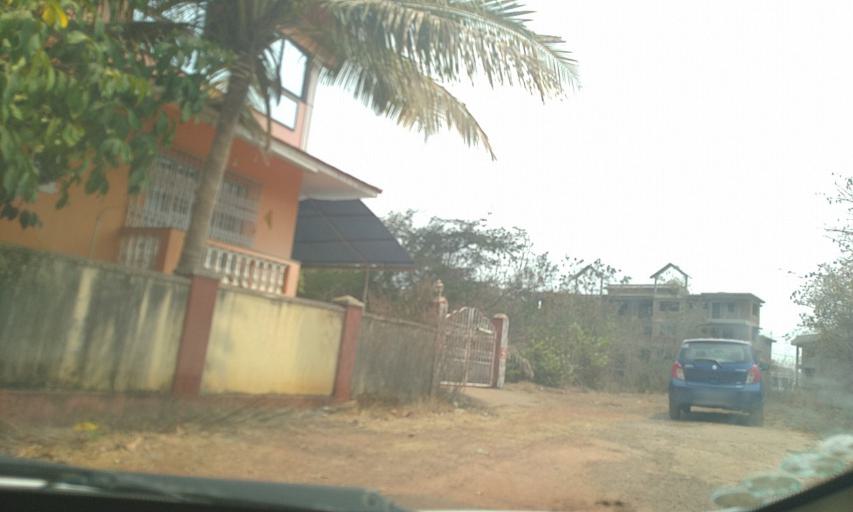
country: IN
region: Goa
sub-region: North Goa
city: Serula
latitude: 15.5398
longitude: 73.8245
